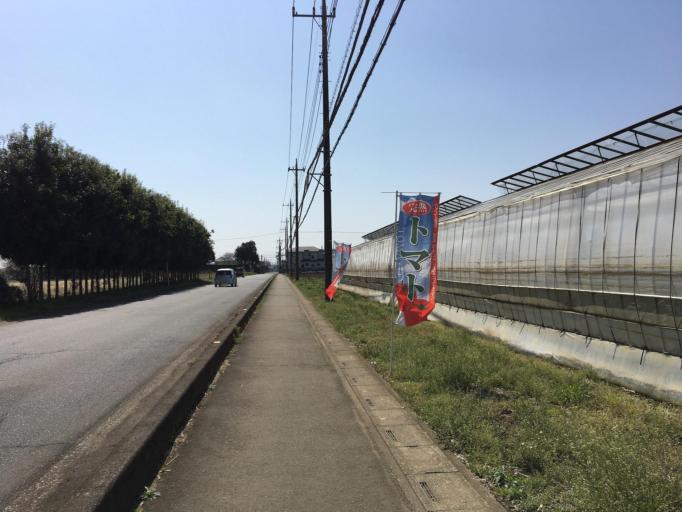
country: JP
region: Saitama
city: Sakado
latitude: 35.9104
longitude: 139.3649
